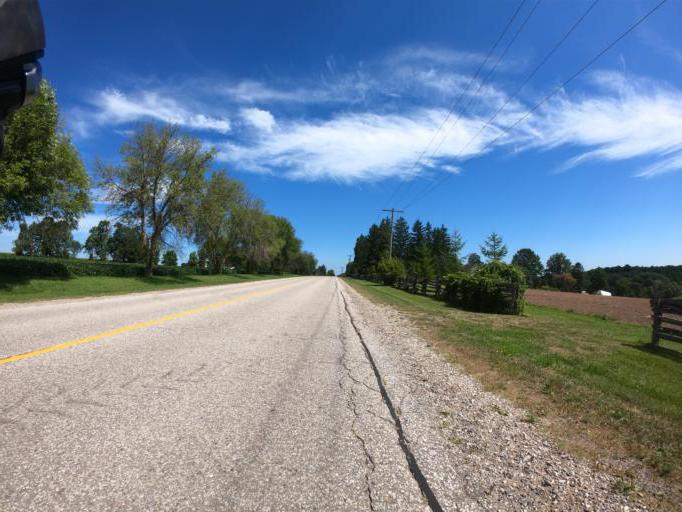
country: CA
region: Ontario
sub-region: Wellington County
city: Guelph
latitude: 43.5527
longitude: -80.3771
